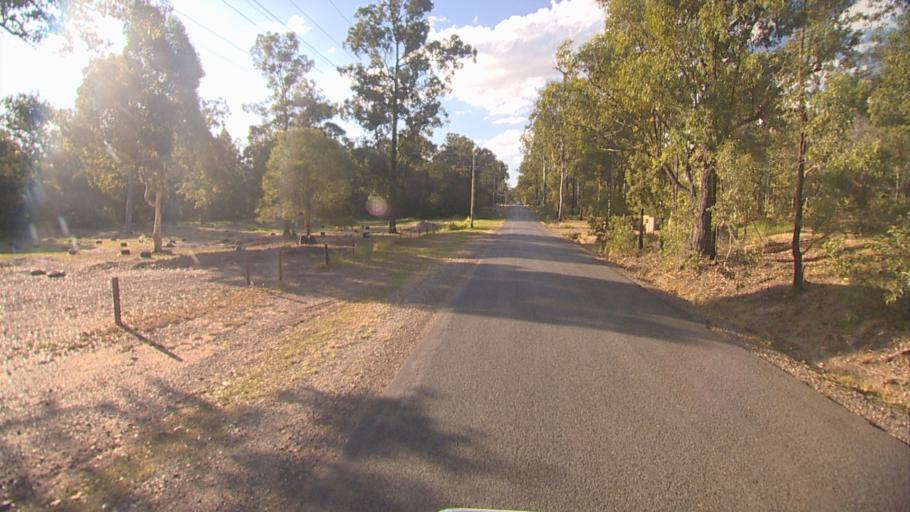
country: AU
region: Queensland
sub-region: Ipswich
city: Springfield Lakes
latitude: -27.6992
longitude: 152.9487
